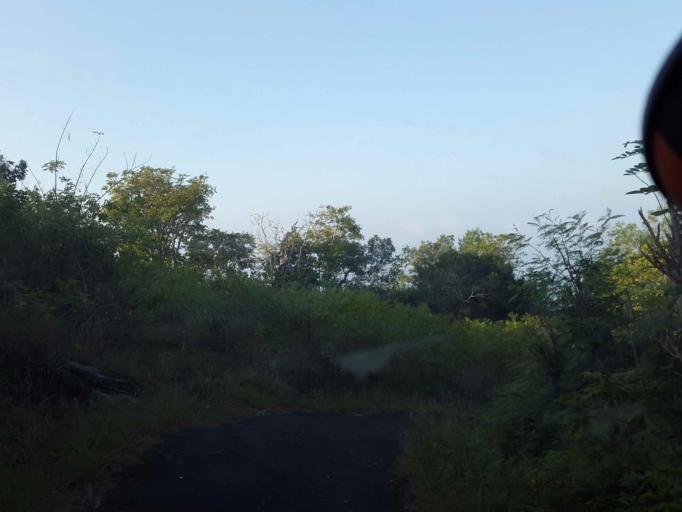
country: ID
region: Bali
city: Suana
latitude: -8.7308
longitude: 115.5887
